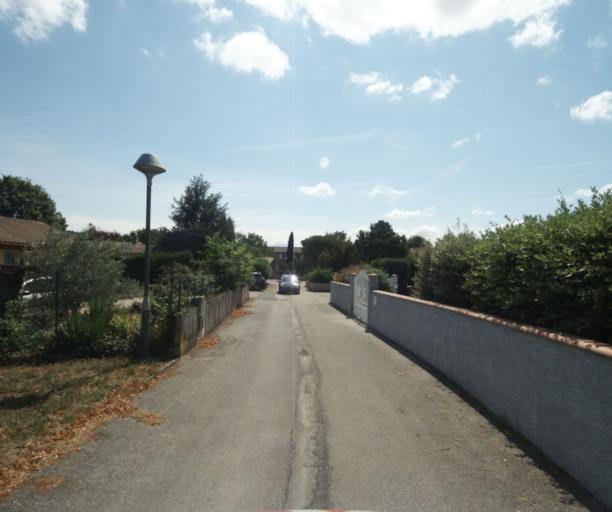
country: FR
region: Midi-Pyrenees
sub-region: Departement de la Haute-Garonne
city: Revel
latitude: 43.4623
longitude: 2.0165
